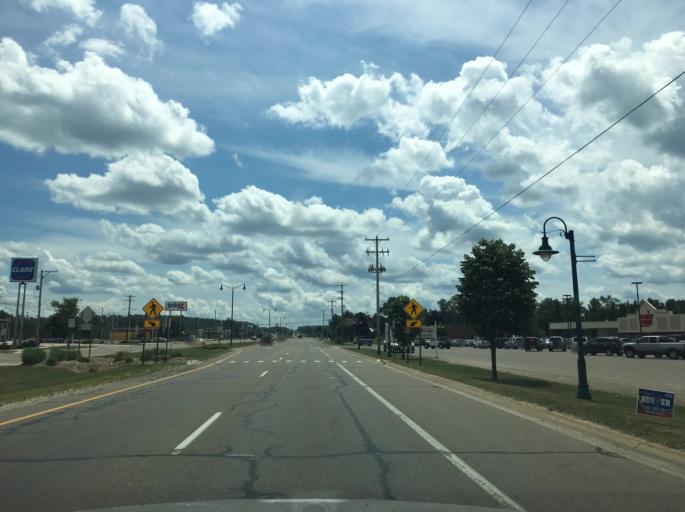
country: US
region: Michigan
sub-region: Crawford County
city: Grayling
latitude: 44.6515
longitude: -84.7086
